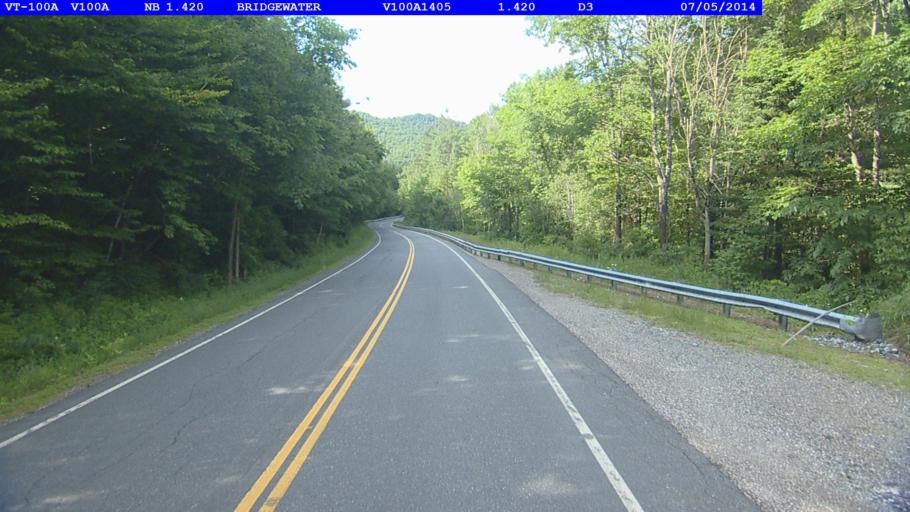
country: US
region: Vermont
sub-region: Windsor County
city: Woodstock
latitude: 43.5387
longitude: -72.7181
